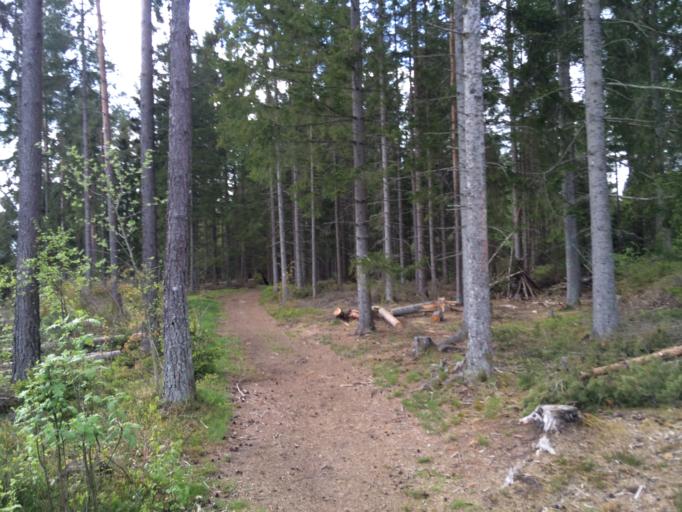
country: SE
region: Vaestra Goetaland
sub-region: Trollhattan
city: Trollhattan
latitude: 58.2249
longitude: 12.2954
